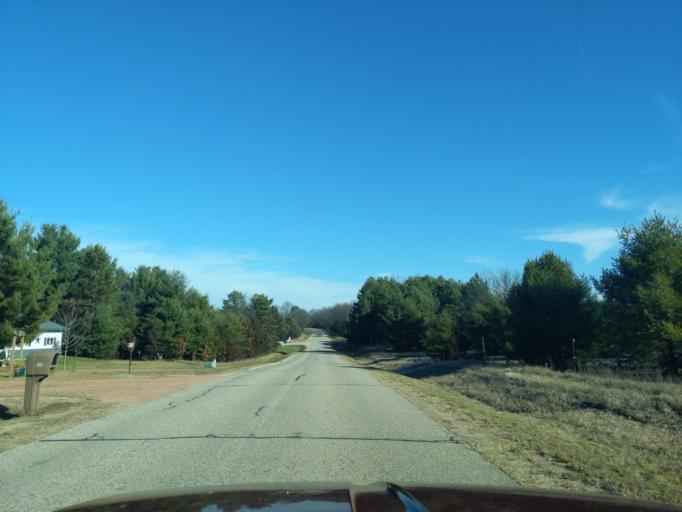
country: US
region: Wisconsin
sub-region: Waushara County
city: Silver Lake
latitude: 44.0879
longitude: -89.1926
